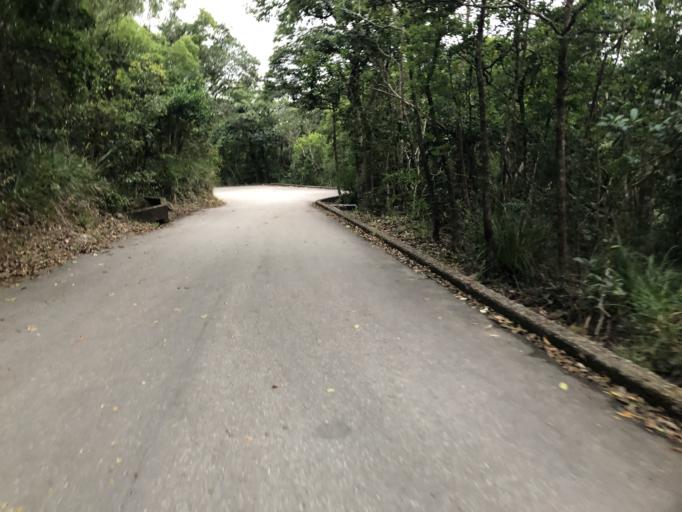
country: HK
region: Wanchai
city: Wan Chai
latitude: 22.2642
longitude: 114.2146
